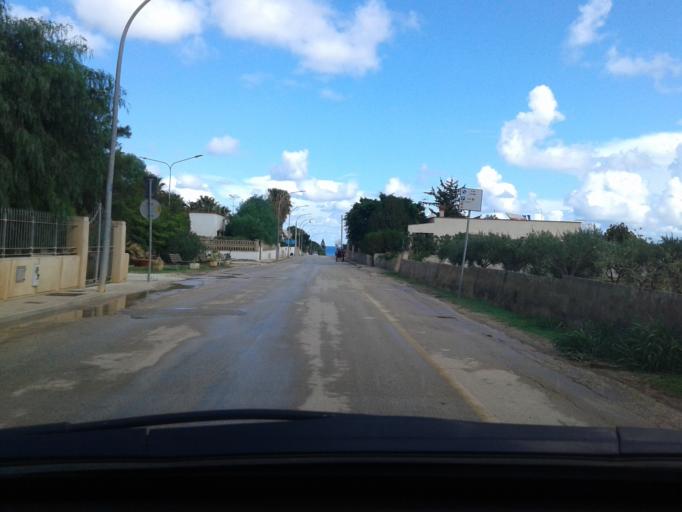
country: IT
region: Sicily
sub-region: Trapani
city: San Vito Lo Capo
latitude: 38.1700
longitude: 12.7422
